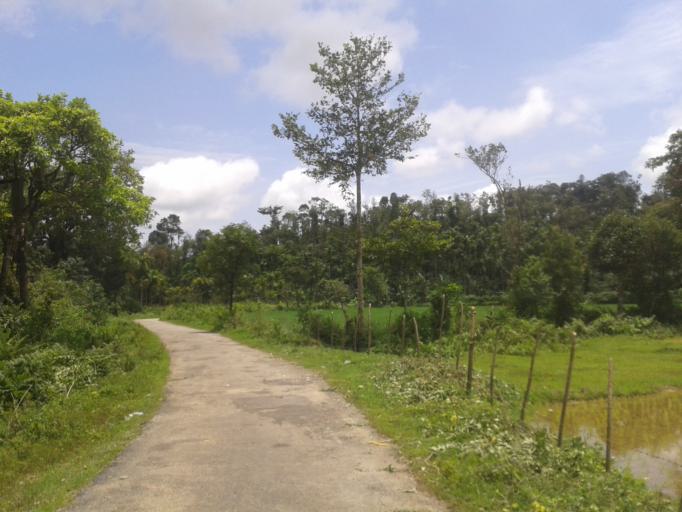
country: IN
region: Karnataka
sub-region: Chikmagalur
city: Mudigere
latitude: 12.9891
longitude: 75.6289
